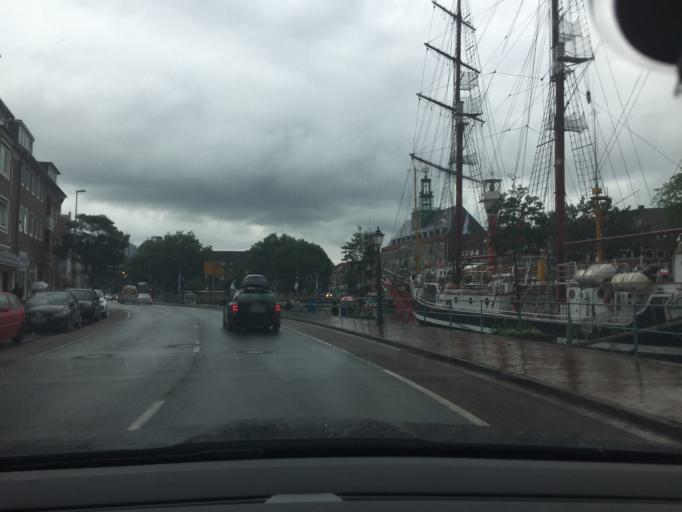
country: DE
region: Lower Saxony
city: Emden
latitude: 53.3652
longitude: 7.2060
